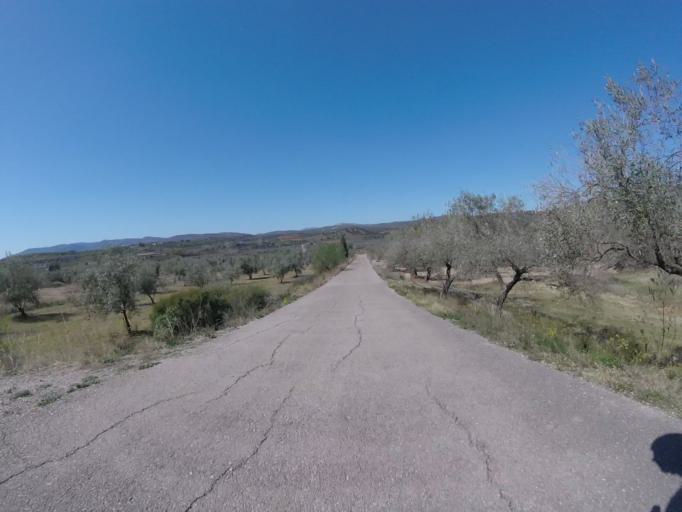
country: ES
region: Valencia
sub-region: Provincia de Castello
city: Cuevas de Vinroma
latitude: 40.3840
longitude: 0.1486
